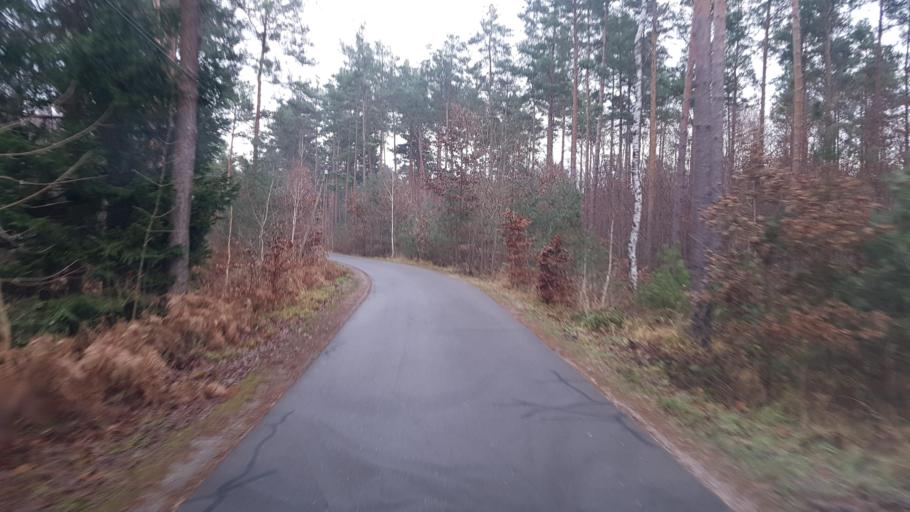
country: DE
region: Brandenburg
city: Plessa
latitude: 51.5270
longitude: 13.6579
